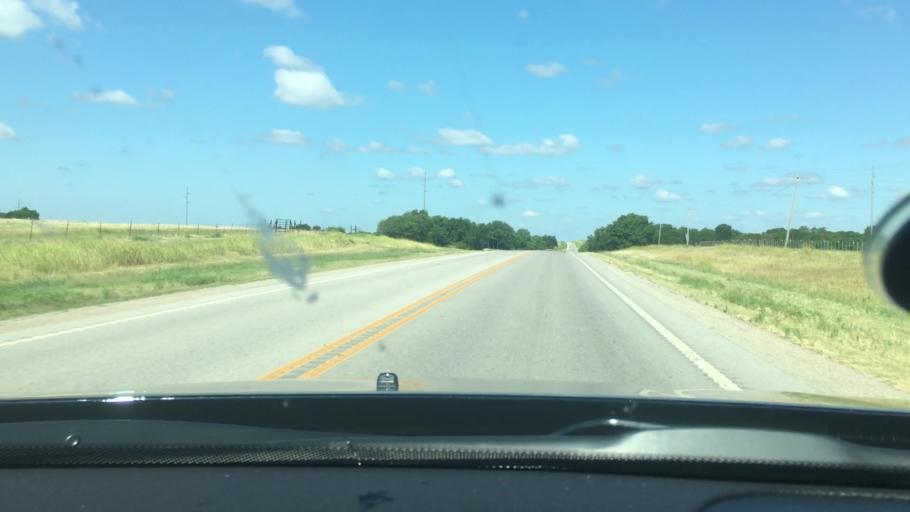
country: US
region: Oklahoma
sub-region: Marshall County
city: Oakland
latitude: 34.0999
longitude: -96.8177
